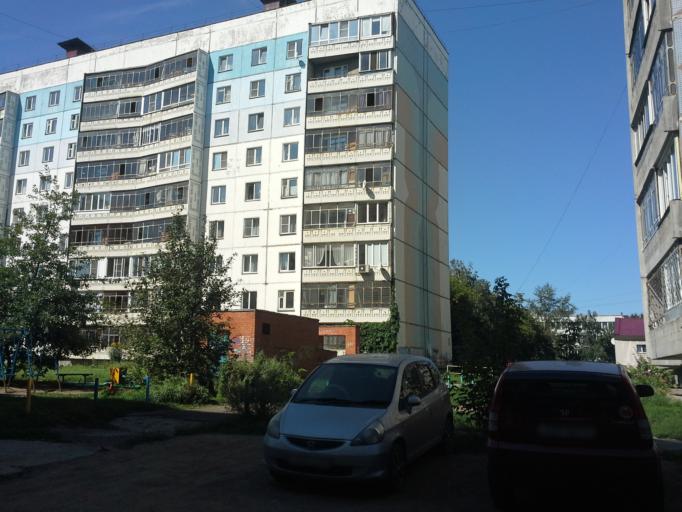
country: RU
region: Novosibirsk
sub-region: Novosibirskiy Rayon
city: Novosibirsk
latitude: 55.0521
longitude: 82.9225
